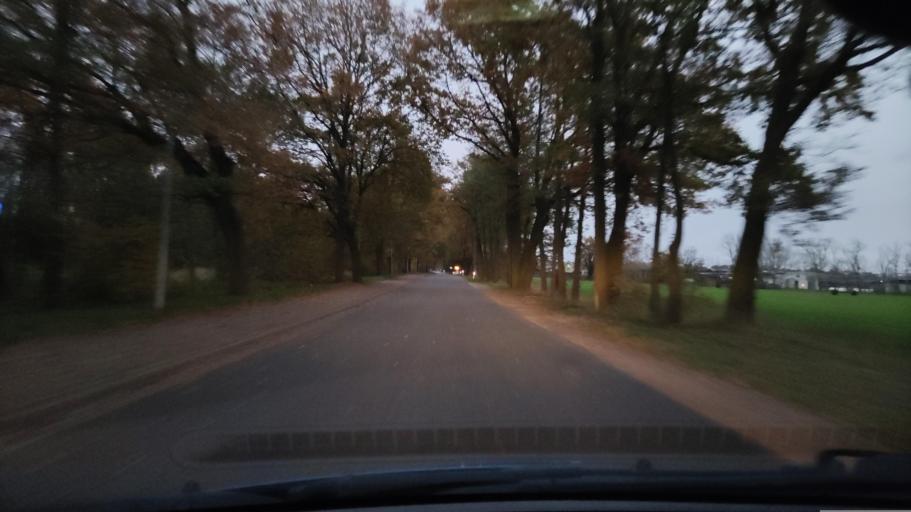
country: DE
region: Mecklenburg-Vorpommern
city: Neu Kaliss
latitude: 53.1810
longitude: 11.2744
